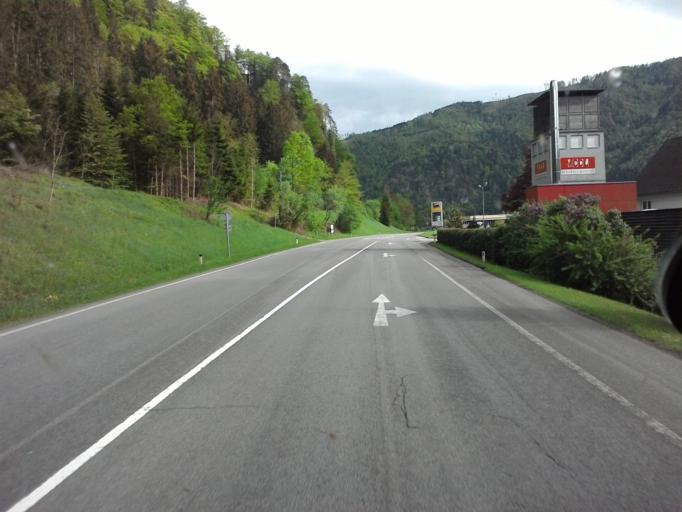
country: AT
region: Styria
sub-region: Politischer Bezirk Liezen
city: Altenmarkt bei Sankt Gallen
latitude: 47.7205
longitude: 14.6536
